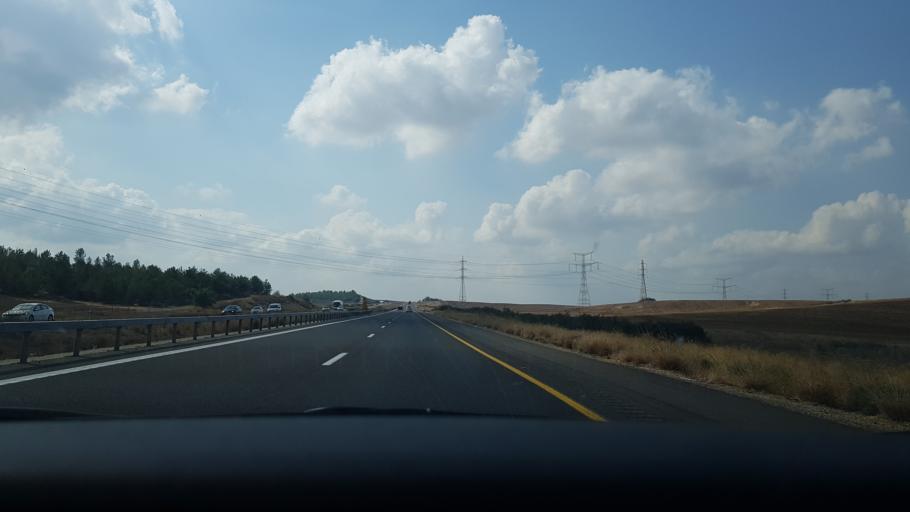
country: IL
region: Southern District
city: Qiryat Gat
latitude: 31.6909
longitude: 34.8121
